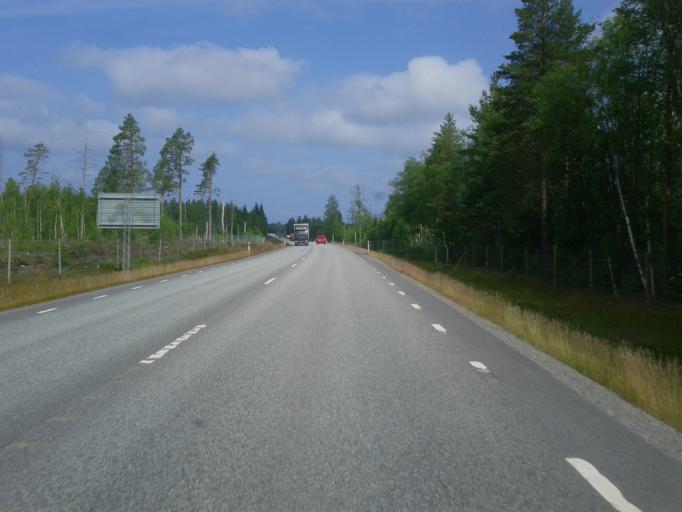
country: SE
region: Vaesterbotten
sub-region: Skelleftea Kommun
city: Burea
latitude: 64.4683
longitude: 21.2930
